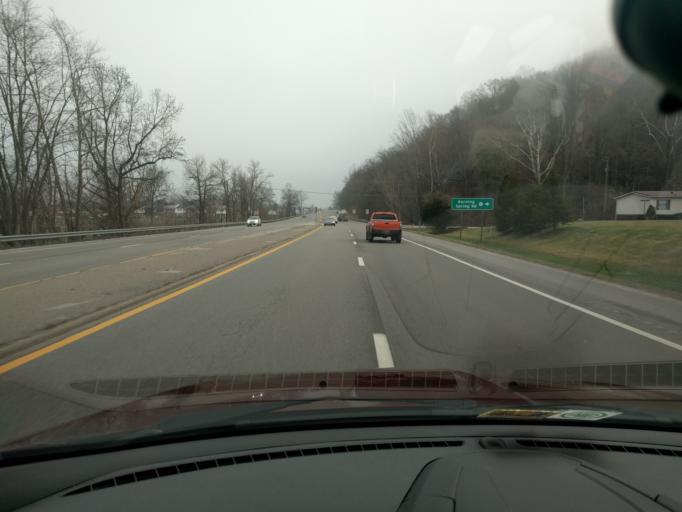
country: US
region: West Virginia
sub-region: Kanawha County
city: Rand
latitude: 38.2685
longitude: -81.5644
